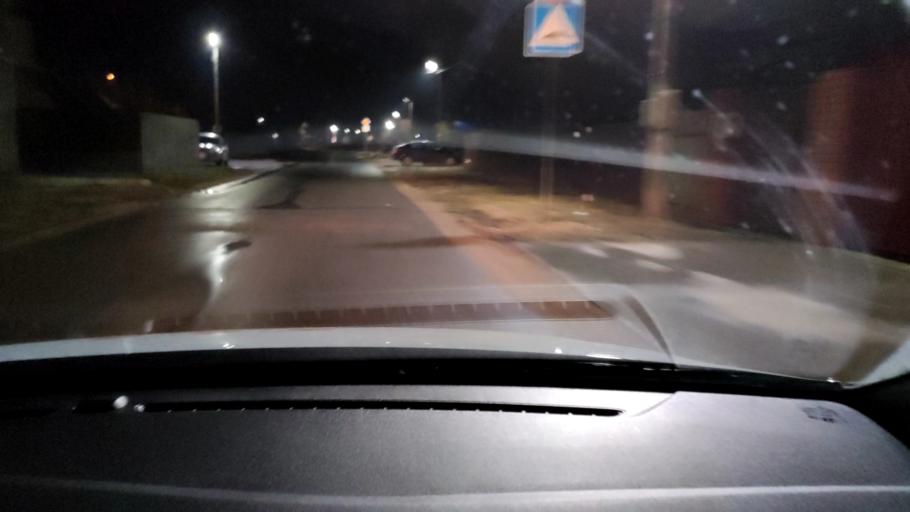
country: RU
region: Tatarstan
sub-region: Gorod Kazan'
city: Kazan
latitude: 55.8975
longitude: 49.1315
